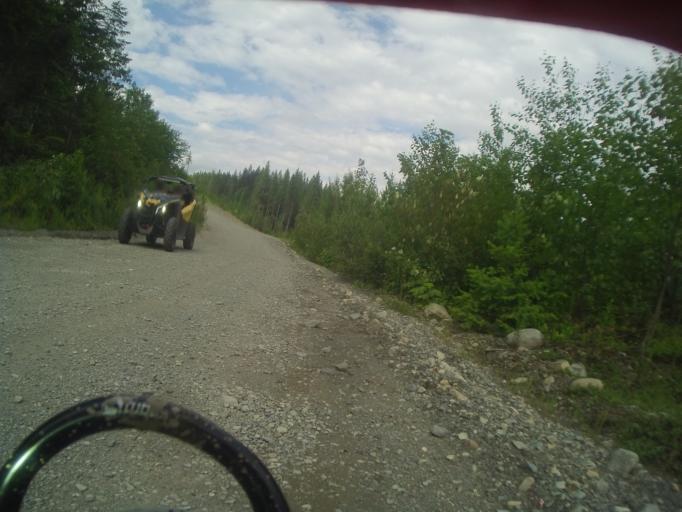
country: CA
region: British Columbia
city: Agassiz
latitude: 49.5395
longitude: -121.8949
